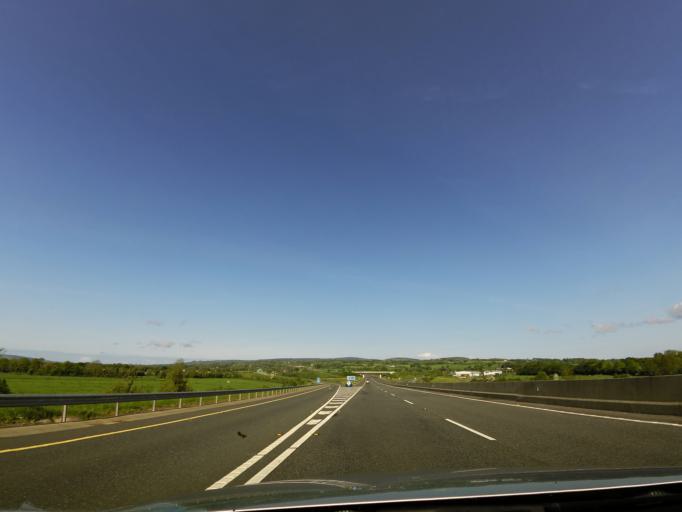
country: IE
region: Munster
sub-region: North Tipperary
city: Nenagh
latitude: 52.8448
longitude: -8.2407
